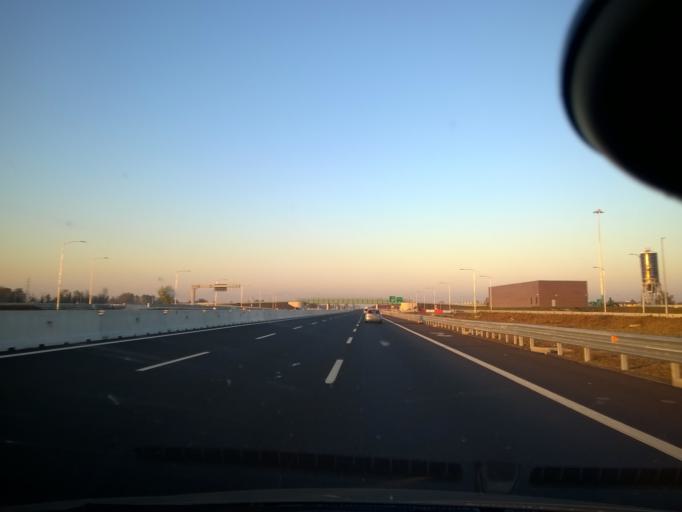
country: IT
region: Lombardy
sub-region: Provincia di Lodi
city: Merlino
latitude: 45.4266
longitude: 9.4213
